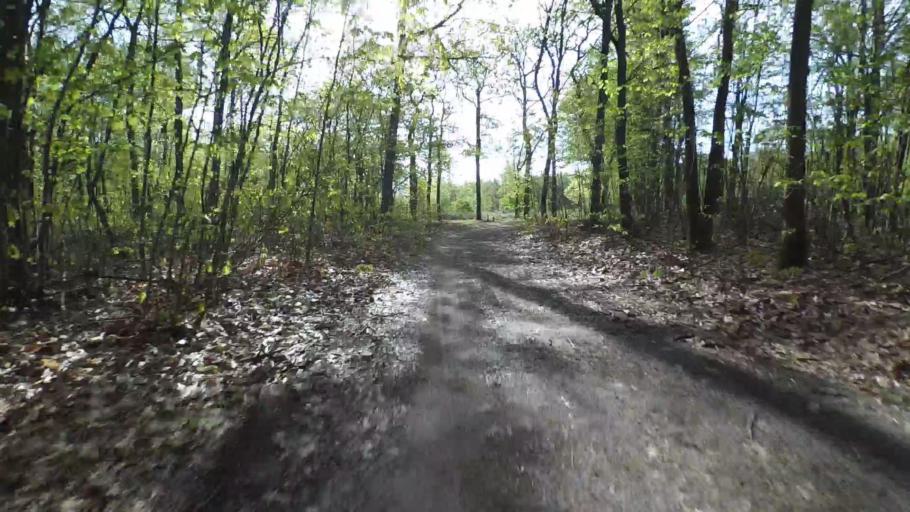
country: NL
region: Utrecht
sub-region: Gemeente Utrechtse Heuvelrug
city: Driebergen-Rijsenburg
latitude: 52.1001
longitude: 5.2931
